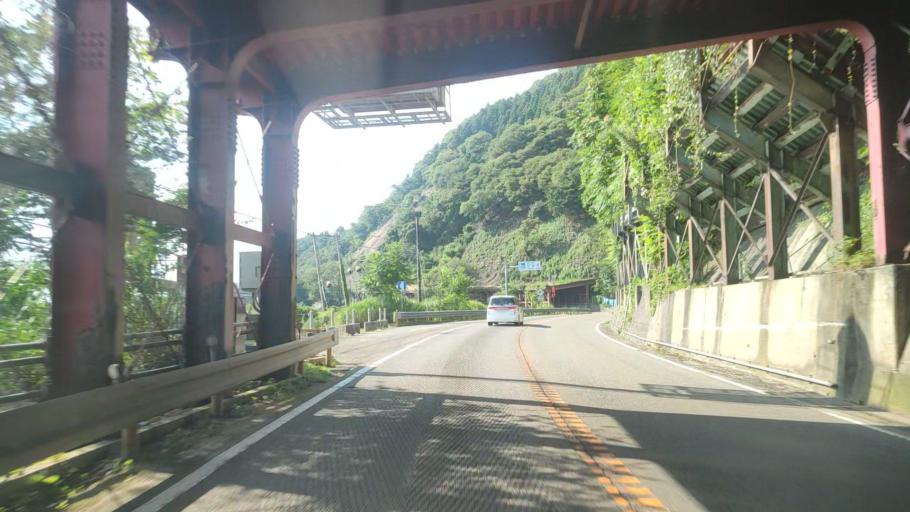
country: JP
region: Fukui
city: Takefu
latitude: 35.7892
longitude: 136.0965
